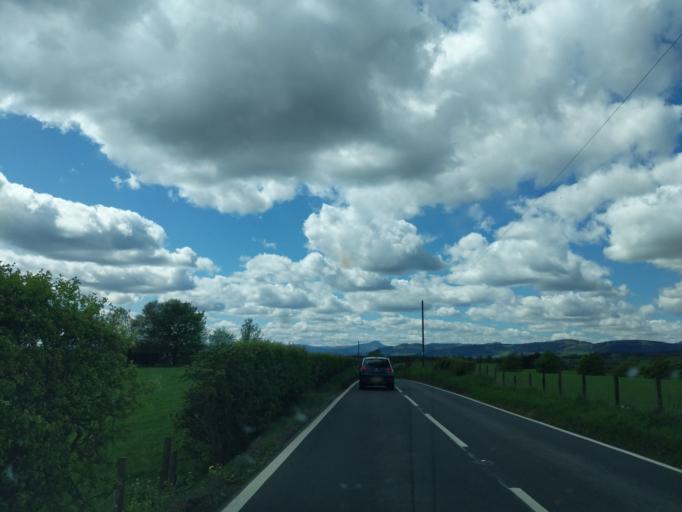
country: GB
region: Scotland
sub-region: Stirling
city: Doune
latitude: 56.1714
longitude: -4.1239
